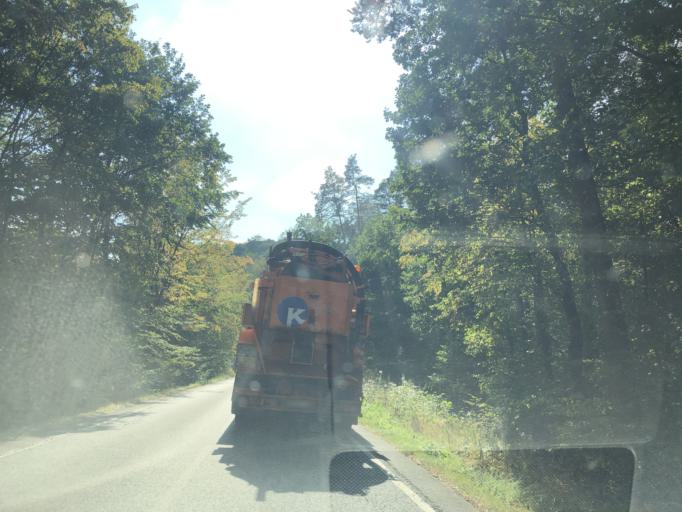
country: DE
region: Hesse
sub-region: Regierungsbezirk Giessen
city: Rauschenberg
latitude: 50.8781
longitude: 8.9512
